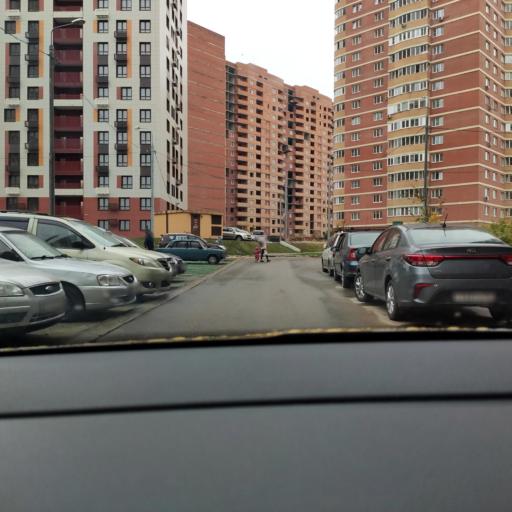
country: RU
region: Moskovskaya
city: Shcherbinka
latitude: 55.4945
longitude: 37.5539
